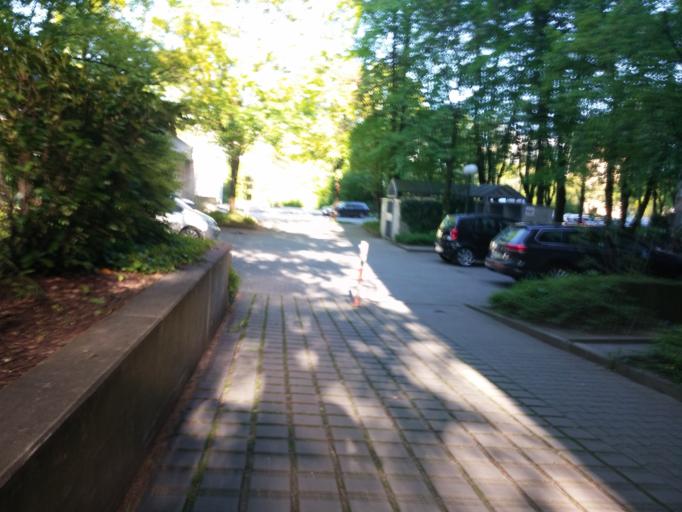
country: DE
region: Bavaria
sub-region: Upper Bavaria
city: Haar
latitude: 48.1070
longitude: 11.7229
